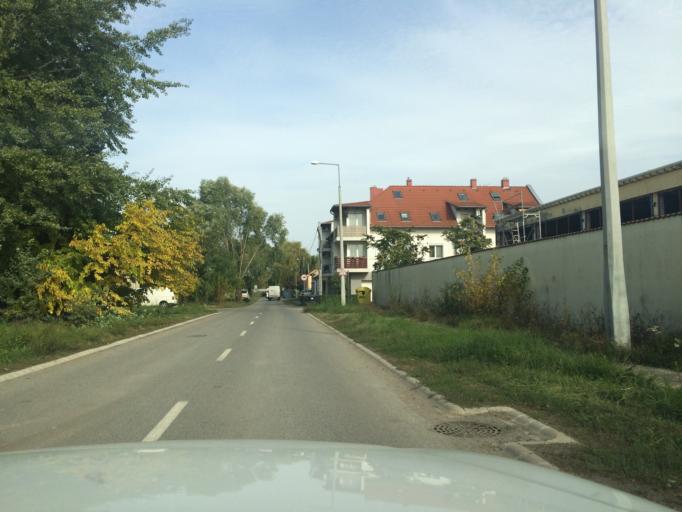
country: HU
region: Szabolcs-Szatmar-Bereg
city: Nyiregyhaza
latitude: 47.9589
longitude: 21.7267
